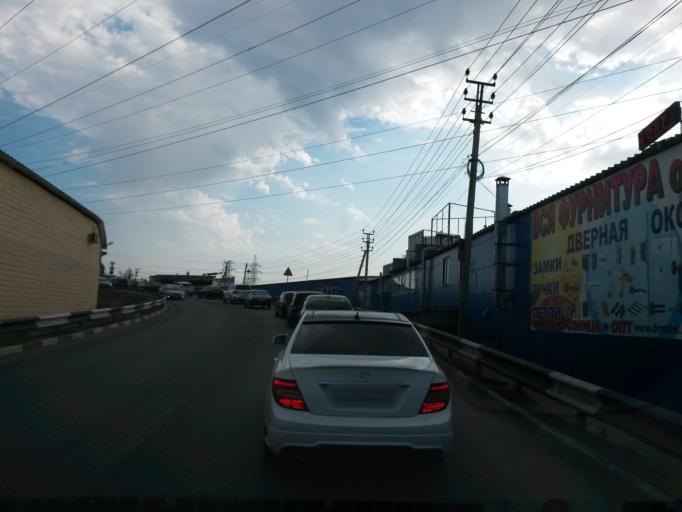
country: RU
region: Moscow
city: Tyoply Stan
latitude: 55.6050
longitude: 37.4821
